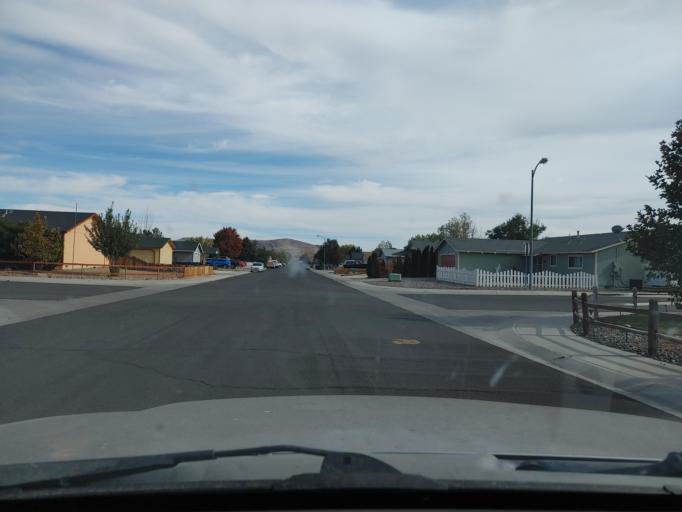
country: US
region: Nevada
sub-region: Lyon County
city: Dayton
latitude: 39.3042
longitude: -119.5397
